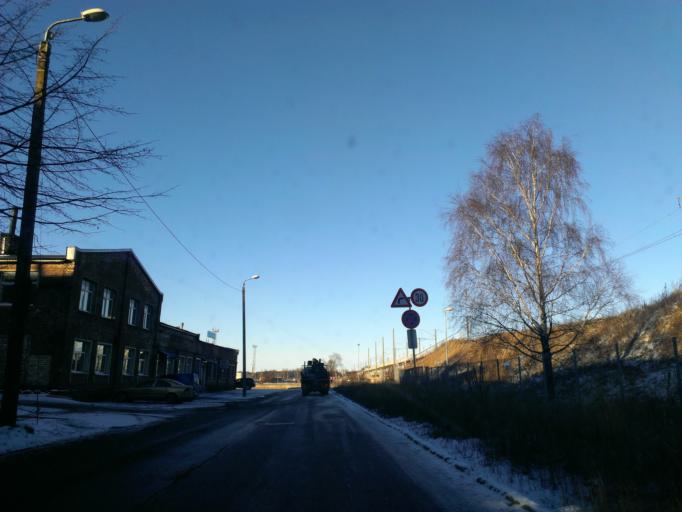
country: LV
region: Riga
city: Jaunciems
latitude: 57.0311
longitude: 24.1344
